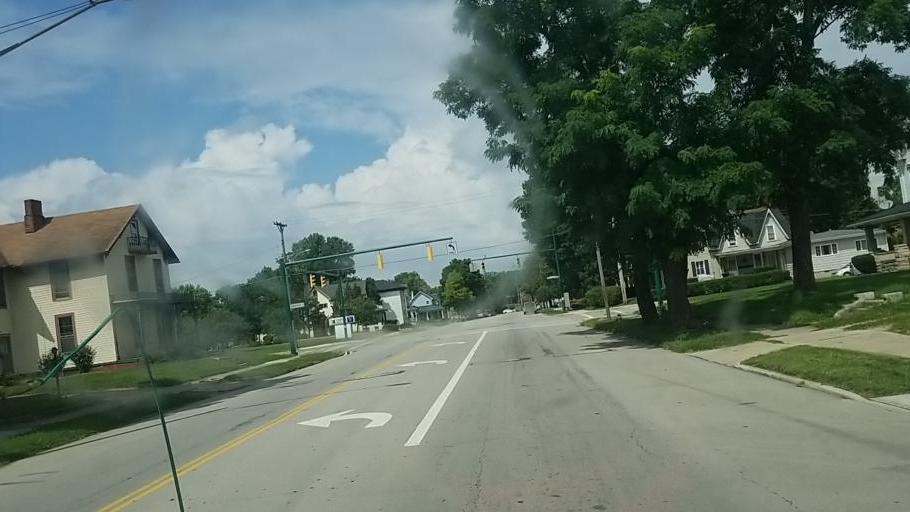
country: US
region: Ohio
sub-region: Champaign County
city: Urbana
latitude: 40.1120
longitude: -83.7520
